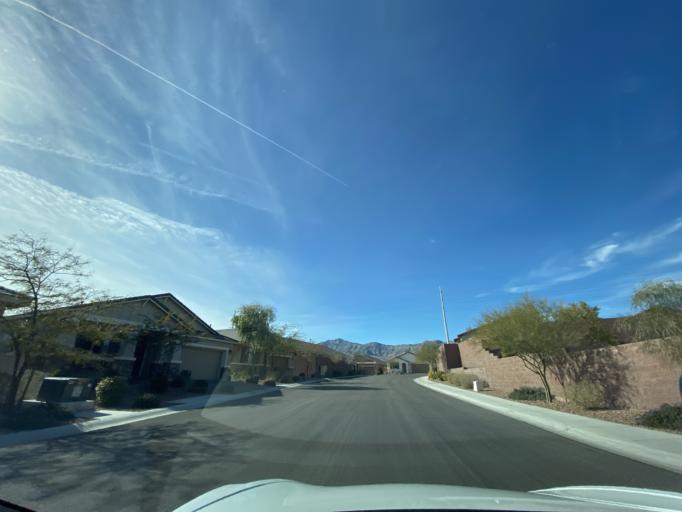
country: US
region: Nevada
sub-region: Clark County
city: Summerlin South
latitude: 36.2912
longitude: -115.3319
